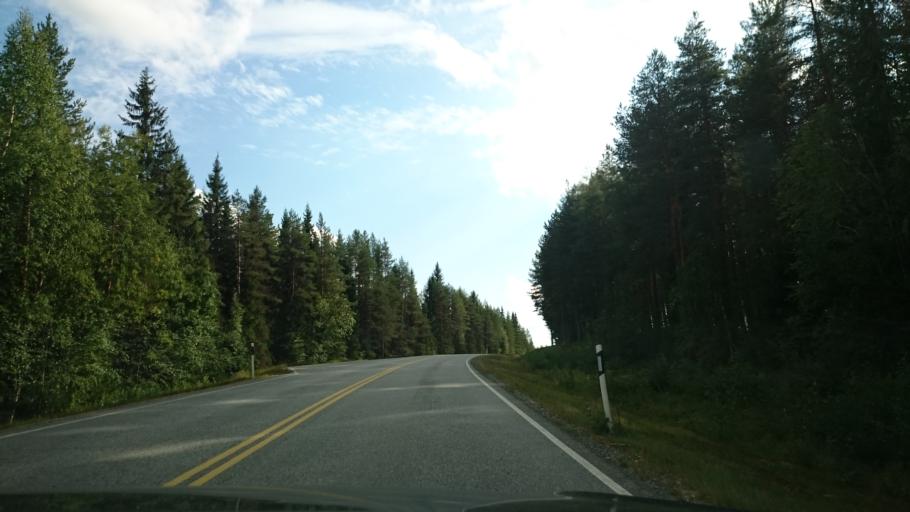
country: FI
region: Kainuu
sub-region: Kehys-Kainuu
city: Kuhmo
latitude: 64.5166
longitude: 29.9447
